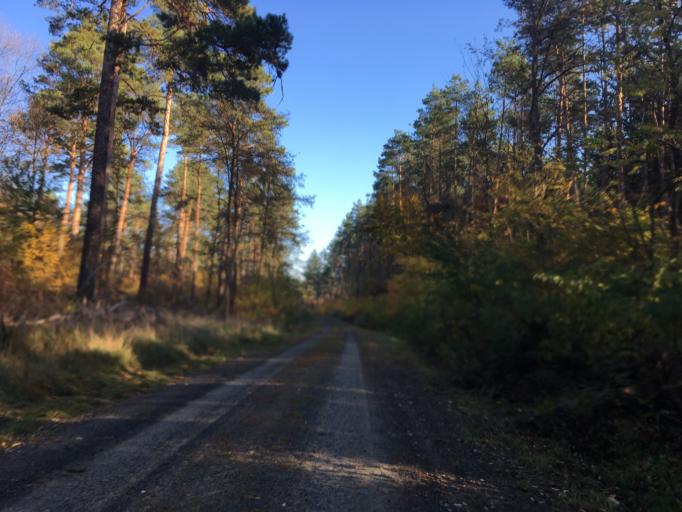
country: DE
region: Brandenburg
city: Wendisch Rietz
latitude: 52.1566
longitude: 13.9756
